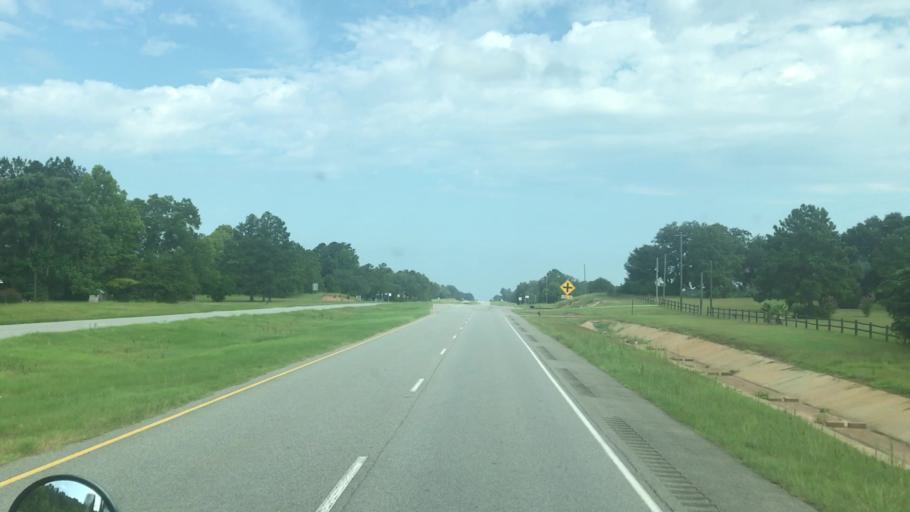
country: US
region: Georgia
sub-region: Early County
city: Blakely
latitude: 31.3017
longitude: -84.8612
